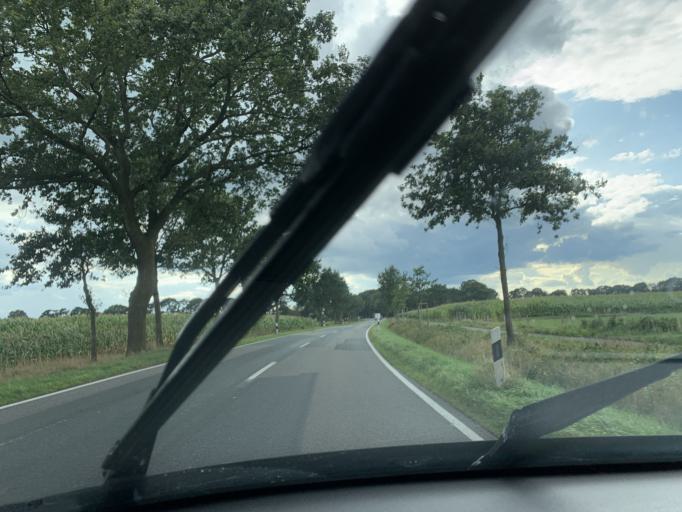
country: DE
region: Lower Saxony
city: Wiefelstede
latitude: 53.2935
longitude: 8.0409
